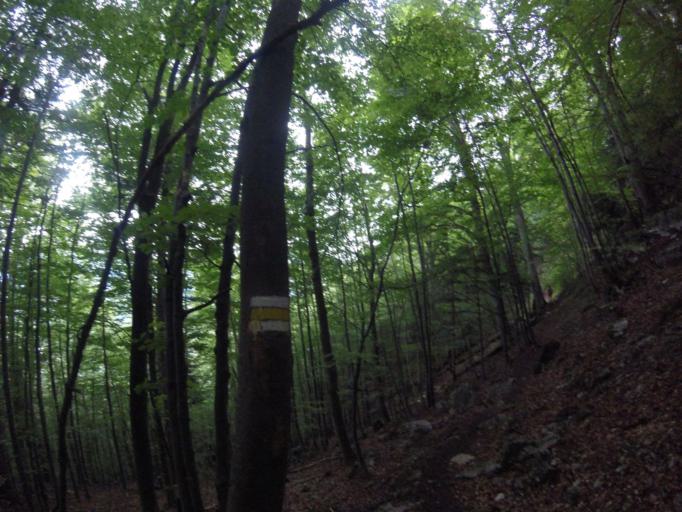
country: SK
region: Zilinsky
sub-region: Okres Zilina
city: Terchova
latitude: 49.2381
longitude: 19.0273
